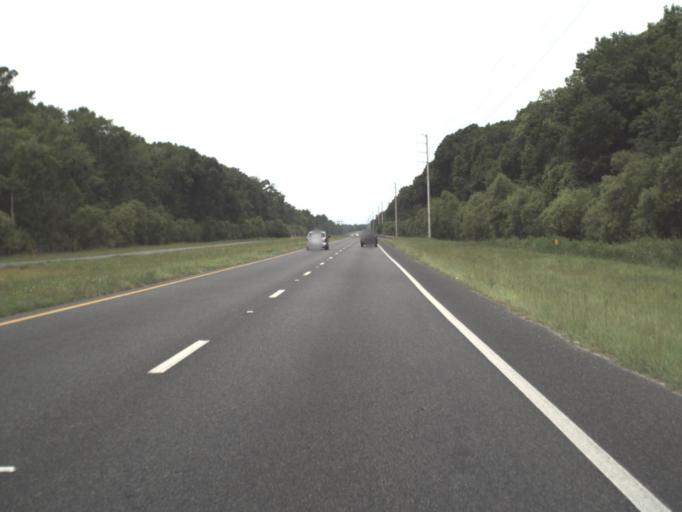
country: US
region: Florida
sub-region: Putnam County
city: Palatka
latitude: 29.6290
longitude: -81.7625
